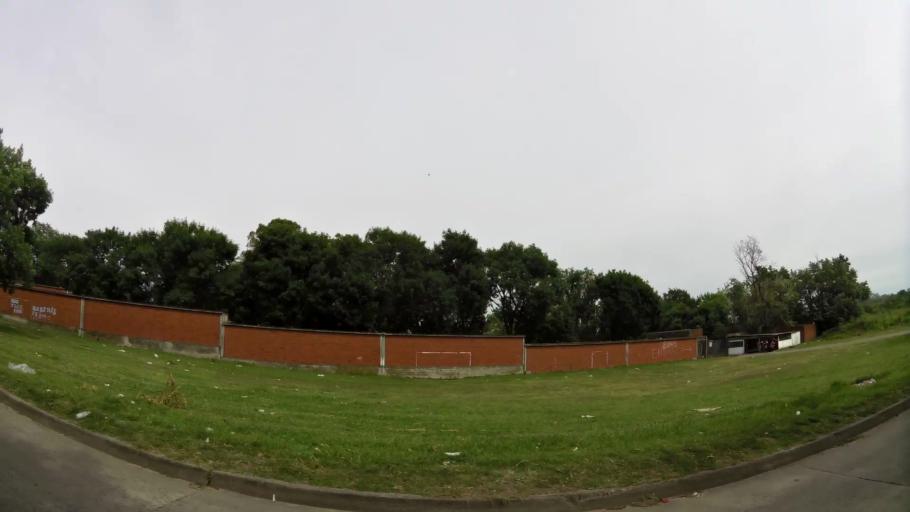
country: UY
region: Montevideo
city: Montevideo
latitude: -34.8419
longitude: -56.1723
